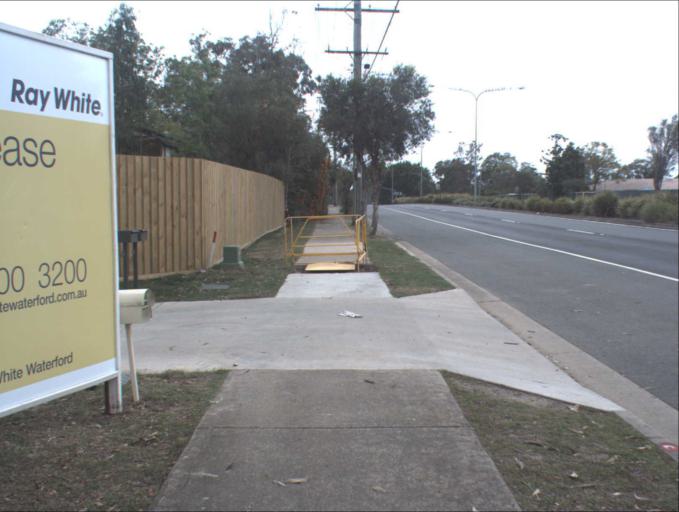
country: AU
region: Queensland
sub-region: Brisbane
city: Ascot
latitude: -27.4104
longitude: 153.0733
